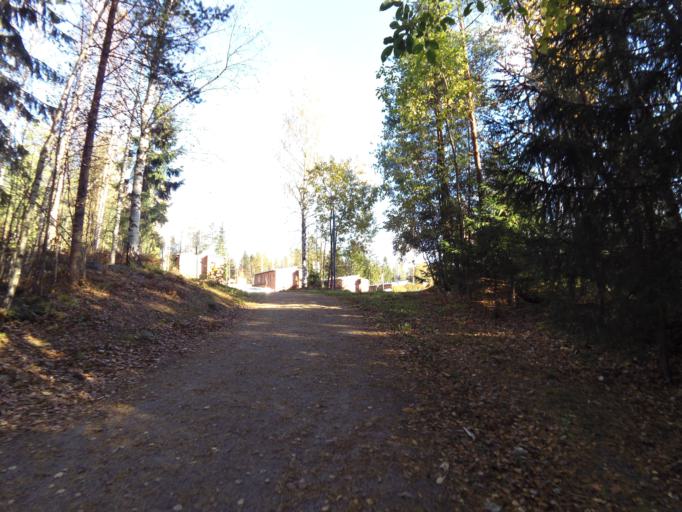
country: FI
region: Uusimaa
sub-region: Helsinki
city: Espoo
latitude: 60.1920
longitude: 24.6772
